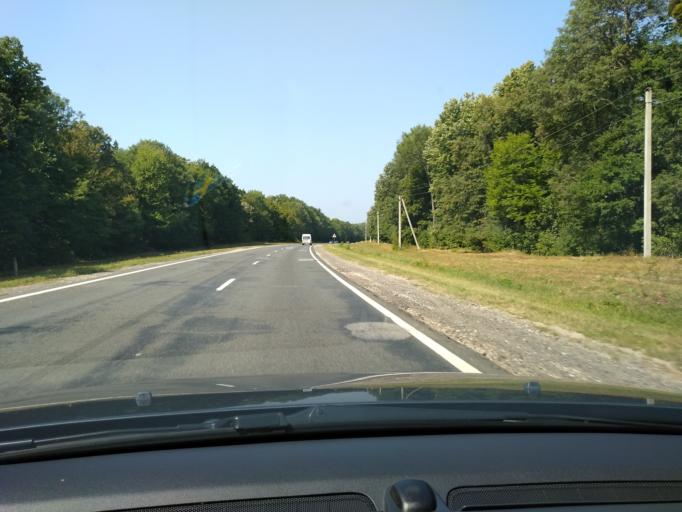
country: MD
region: Straseni
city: Straseni
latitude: 47.0799
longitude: 28.5097
